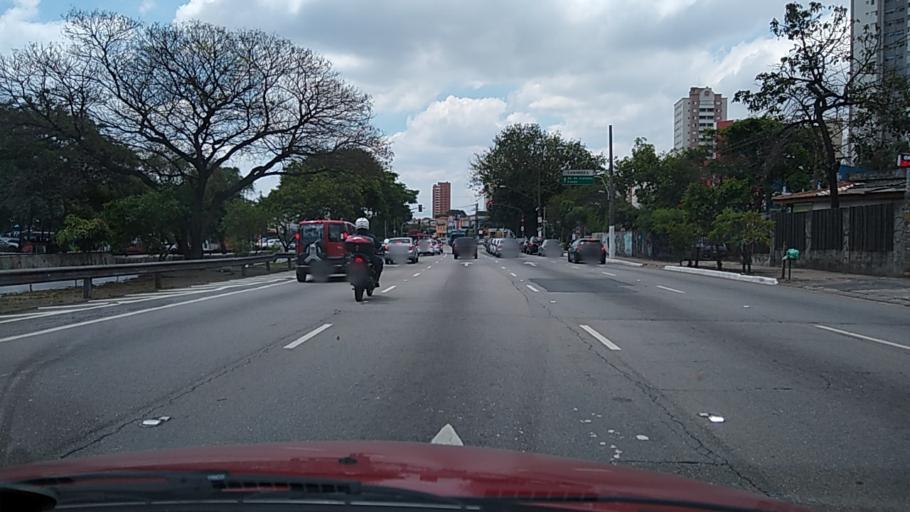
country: BR
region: Sao Paulo
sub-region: Diadema
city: Diadema
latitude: -23.6169
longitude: -46.6273
